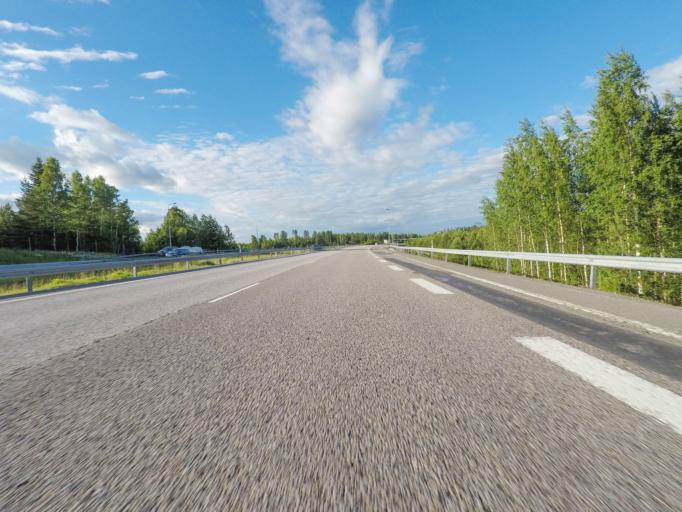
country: FI
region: Paijanne Tavastia
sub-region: Lahti
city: Hollola
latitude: 60.8228
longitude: 25.5201
